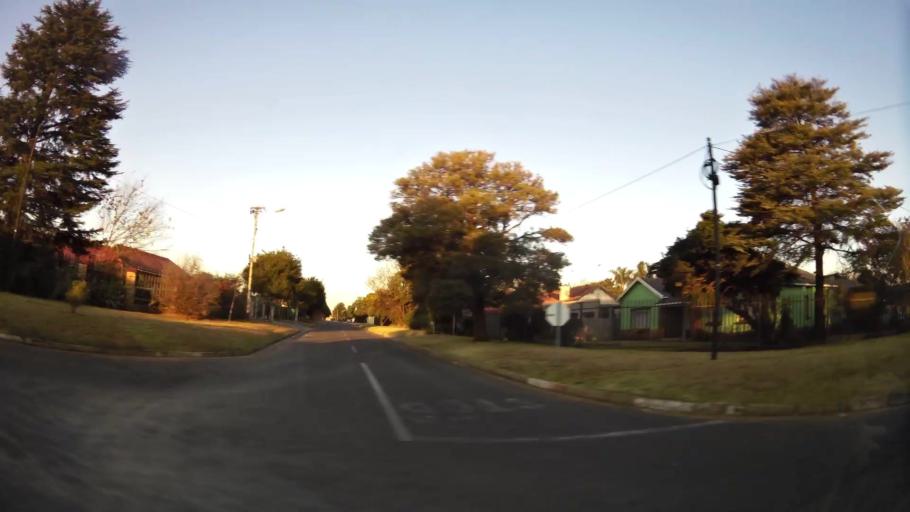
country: ZA
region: Gauteng
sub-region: City of Johannesburg Metropolitan Municipality
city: Roodepoort
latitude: -26.1471
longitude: 27.8823
